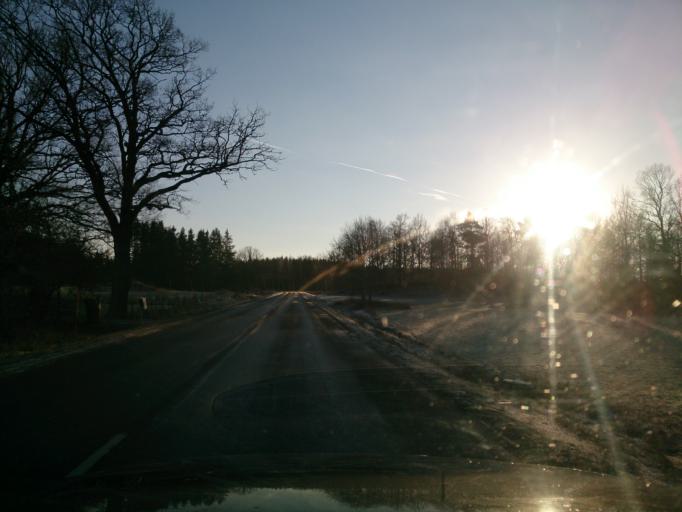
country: SE
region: OEstergoetland
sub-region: Atvidabergs Kommun
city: Atvidaberg
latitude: 58.3645
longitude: 16.0249
